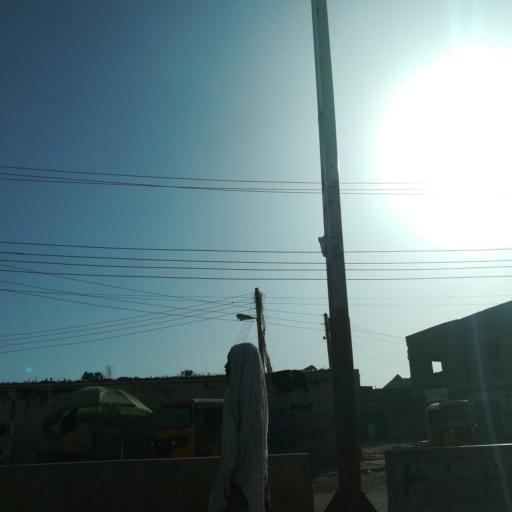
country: NG
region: Kano
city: Kano
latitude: 12.0154
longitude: 8.4969
